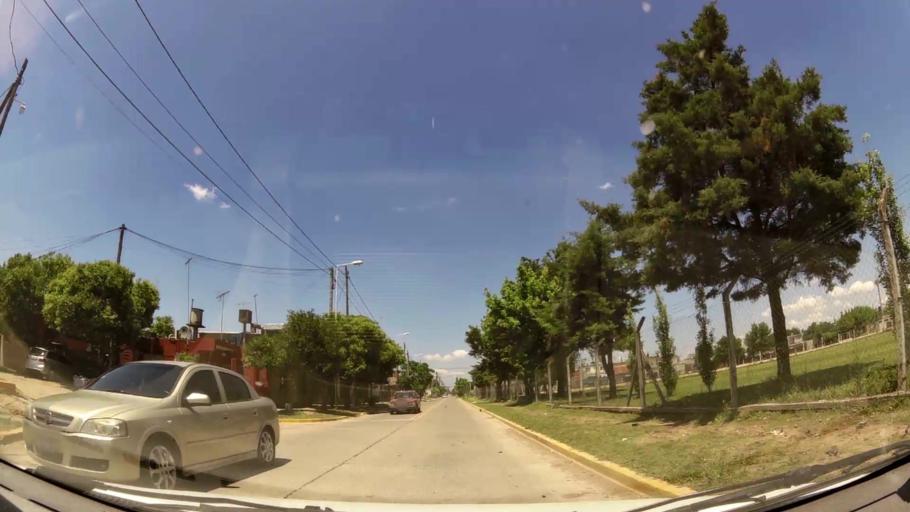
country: AR
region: Buenos Aires
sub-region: Partido de Merlo
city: Merlo
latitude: -34.6445
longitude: -58.7260
